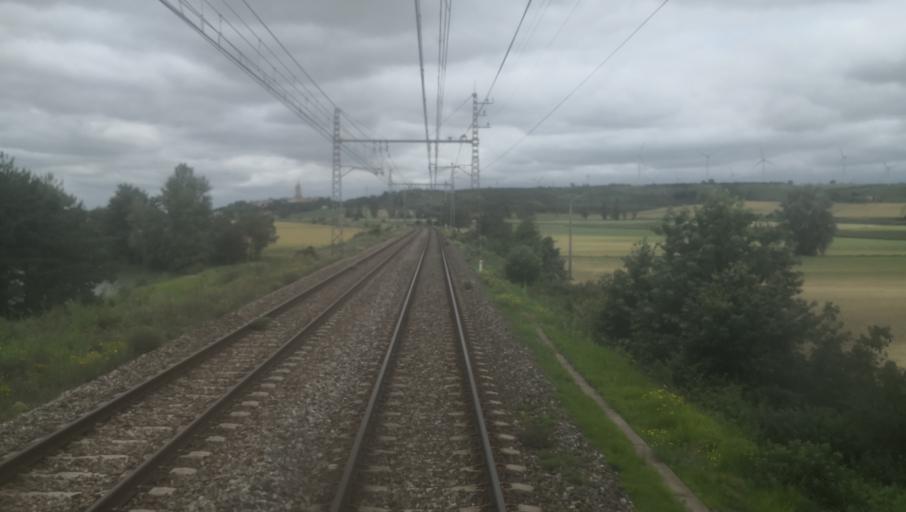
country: FR
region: Midi-Pyrenees
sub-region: Departement de la Haute-Garonne
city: Avignonet-Lauragais
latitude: 43.3576
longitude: 1.8057
